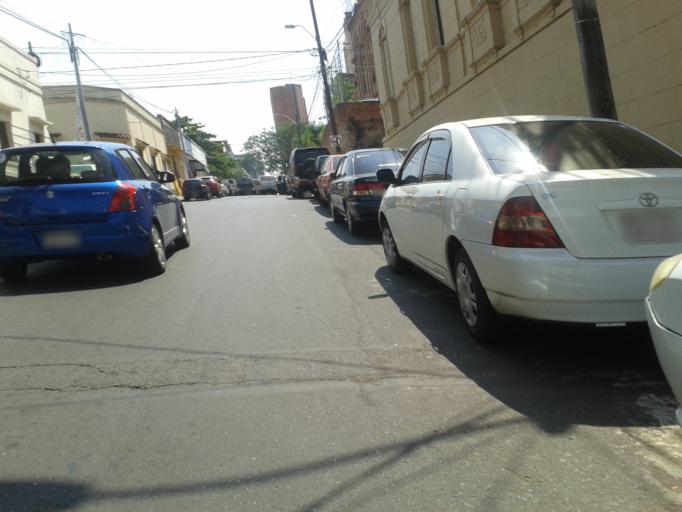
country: PY
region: Asuncion
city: Asuncion
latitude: -25.2850
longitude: -57.6397
